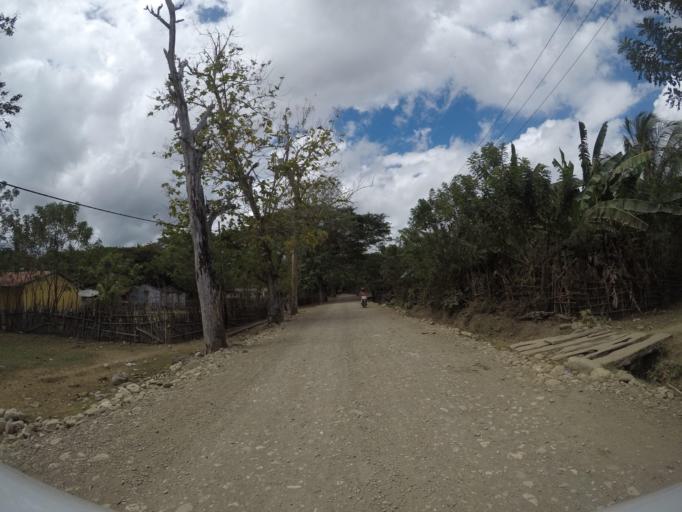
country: TL
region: Lautem
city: Lospalos
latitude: -8.5142
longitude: 126.8347
